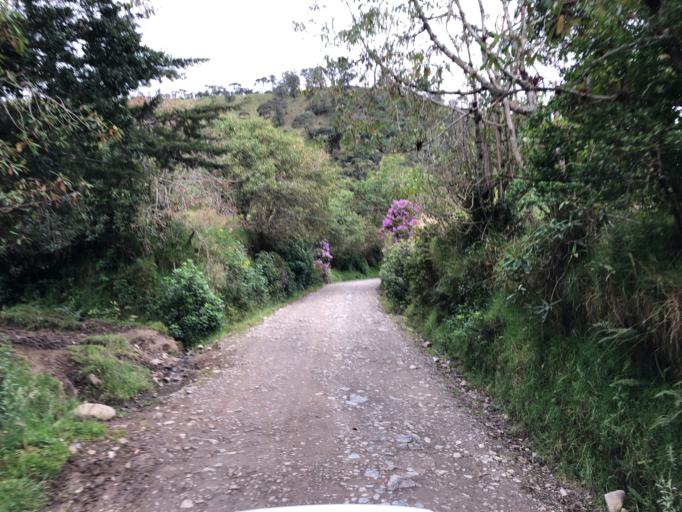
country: CO
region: Cauca
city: Totoro
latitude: 2.5023
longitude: -76.3577
